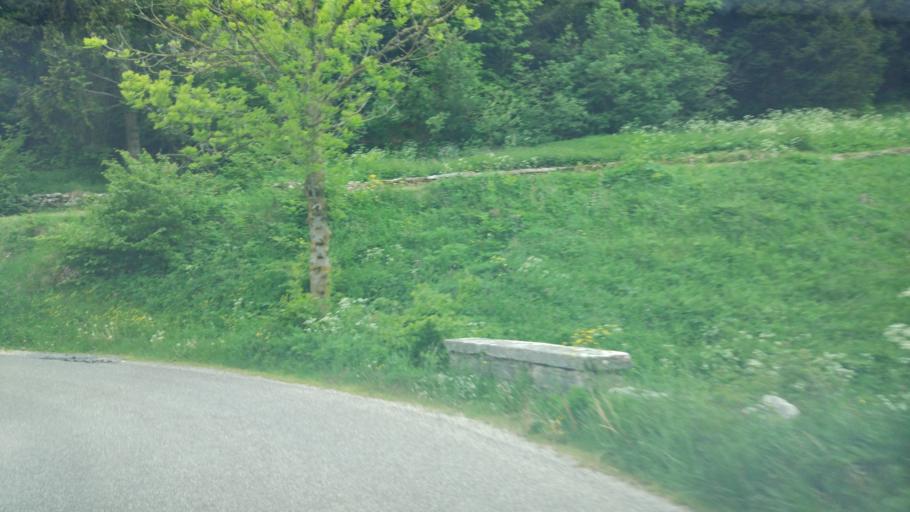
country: IT
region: Veneto
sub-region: Provincia di Verona
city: Erbezzo
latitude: 45.6546
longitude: 11.0011
